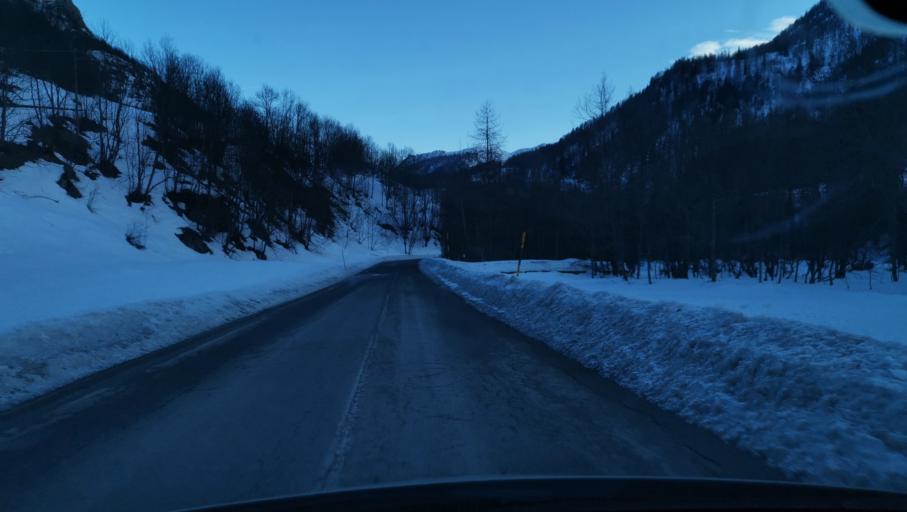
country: IT
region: Piedmont
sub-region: Provincia di Cuneo
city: Bersezio
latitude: 44.3639
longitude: 6.9916
